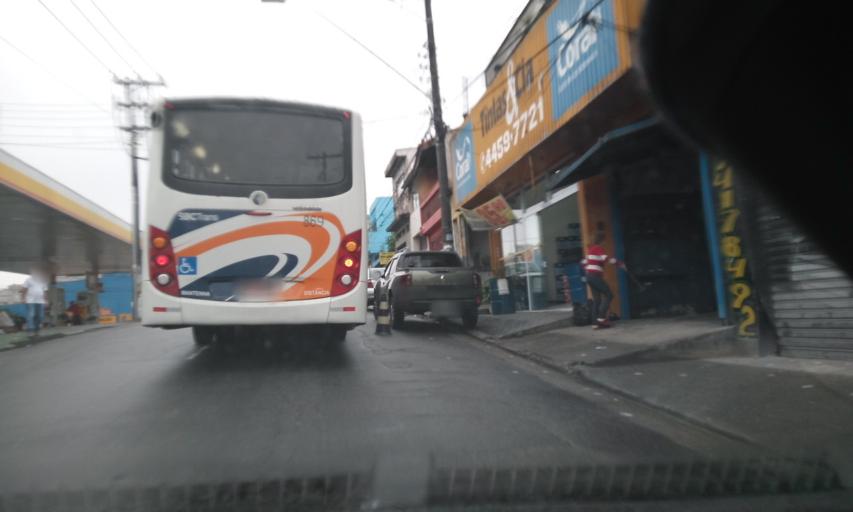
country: BR
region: Sao Paulo
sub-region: Santo Andre
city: Santo Andre
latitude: -23.7016
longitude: -46.5193
